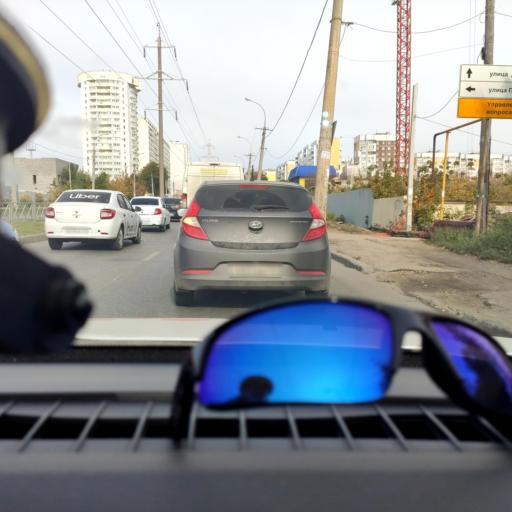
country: RU
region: Samara
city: Samara
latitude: 53.2044
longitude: 50.2139
